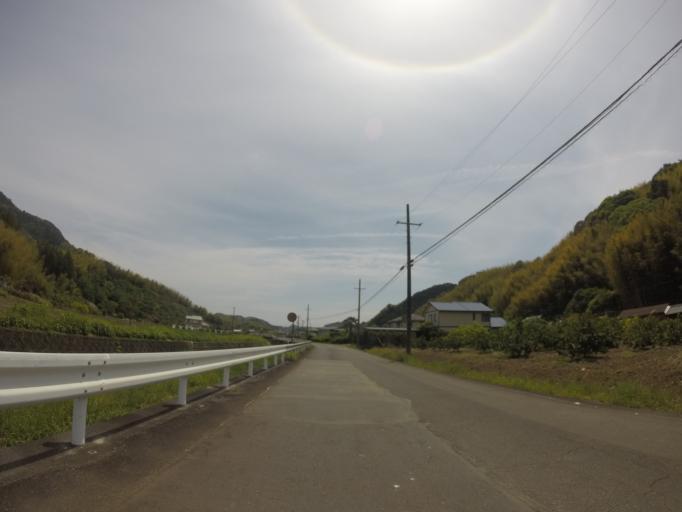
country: JP
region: Shizuoka
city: Fujieda
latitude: 34.9294
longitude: 138.2323
